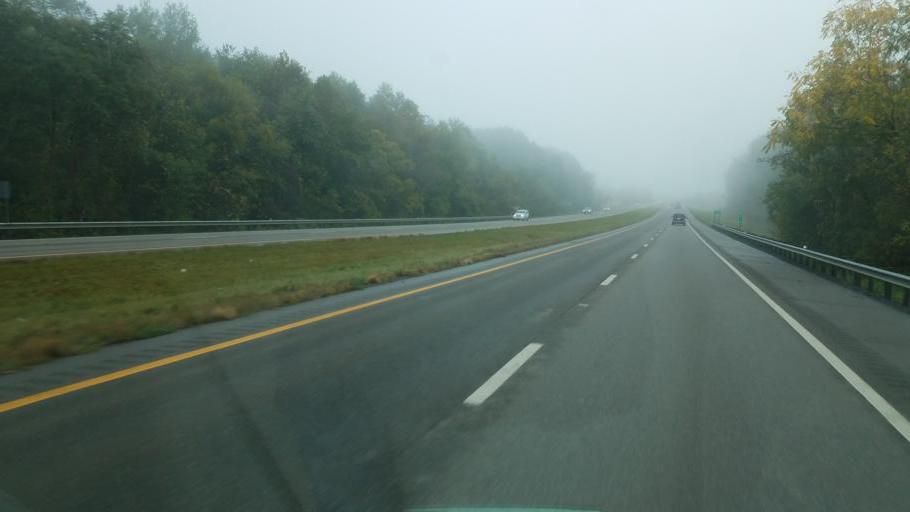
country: US
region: Ohio
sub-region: Tuscarawas County
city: New Philadelphia
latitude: 40.4634
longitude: -81.4225
